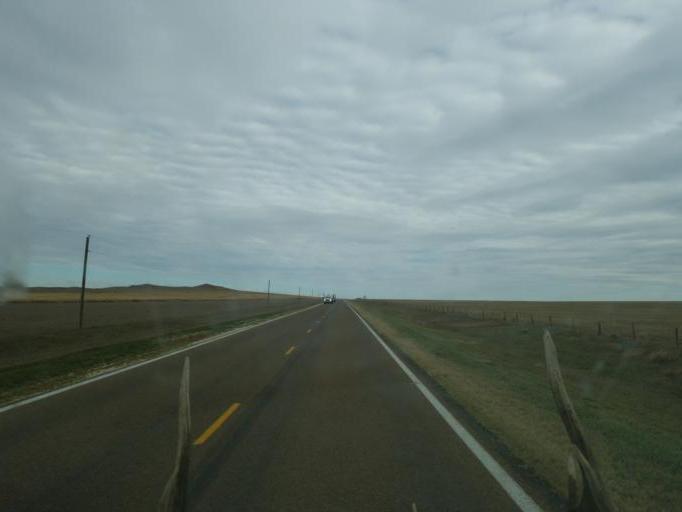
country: US
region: Kansas
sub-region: Wallace County
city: Sharon Springs
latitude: 39.0042
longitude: -101.3865
